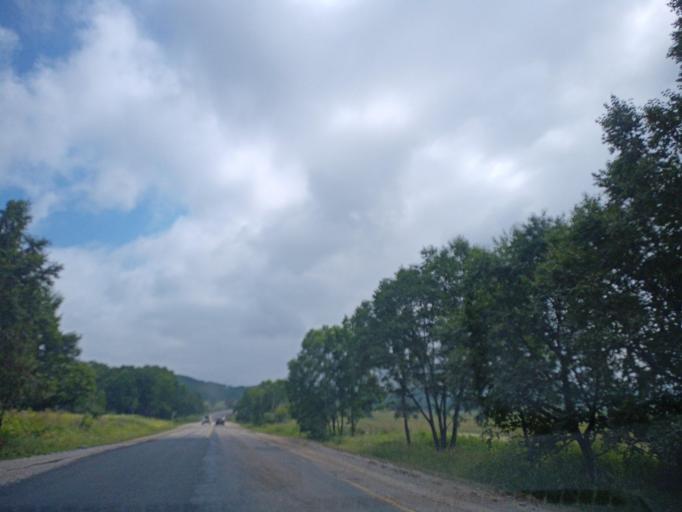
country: RU
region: Primorskiy
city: Dal'nerechensk
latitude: 46.0355
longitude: 133.8642
